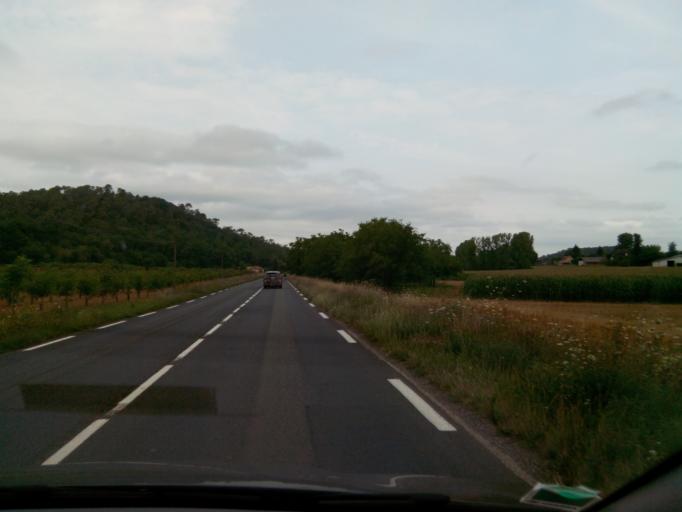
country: FR
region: Aquitaine
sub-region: Departement de la Dordogne
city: Carsac-Aillac
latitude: 44.8559
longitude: 1.3003
